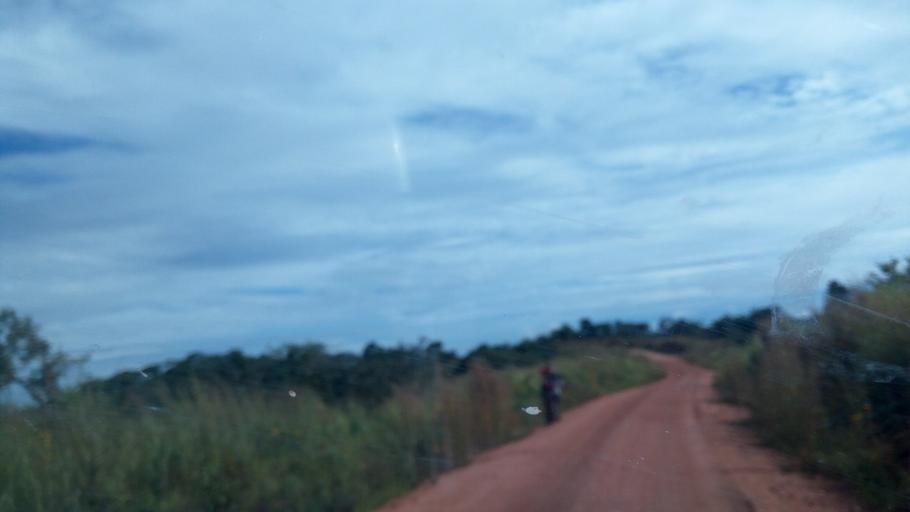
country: CD
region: Katanga
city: Kalemie
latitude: -6.1543
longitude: 28.8888
